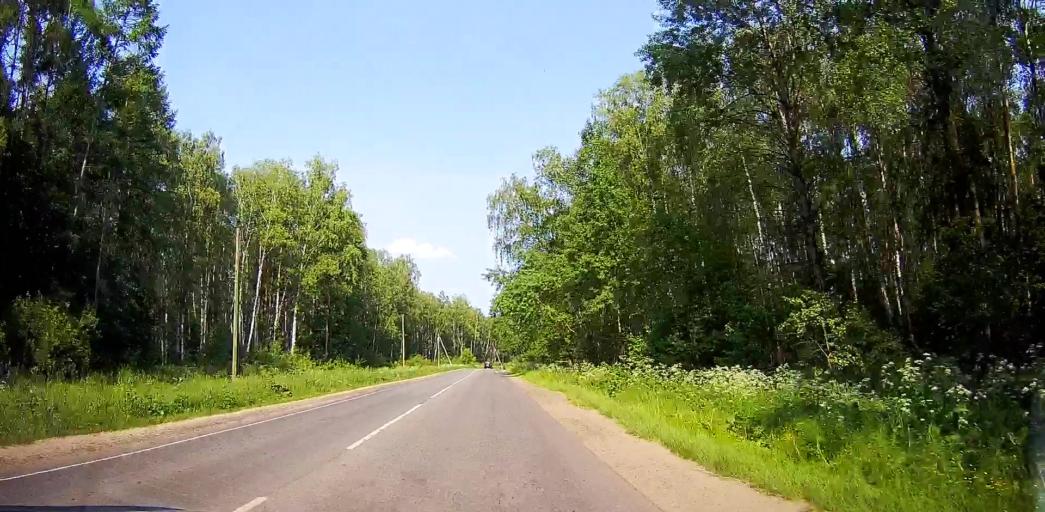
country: RU
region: Moskovskaya
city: Barybino
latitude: 55.2834
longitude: 37.9247
